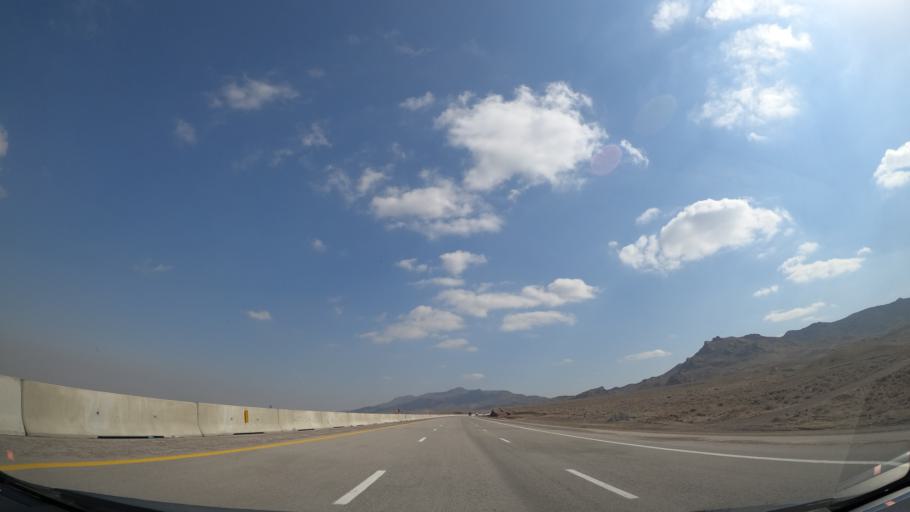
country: IR
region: Alborz
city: Eshtehard
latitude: 35.7069
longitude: 50.6071
